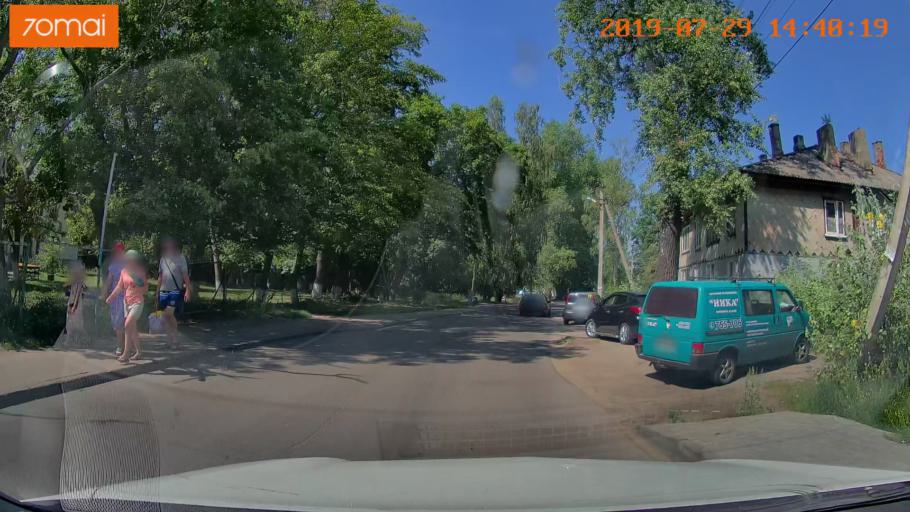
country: RU
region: Kaliningrad
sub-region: Gorod Kaliningrad
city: Baltiysk
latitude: 54.6542
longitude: 19.9015
